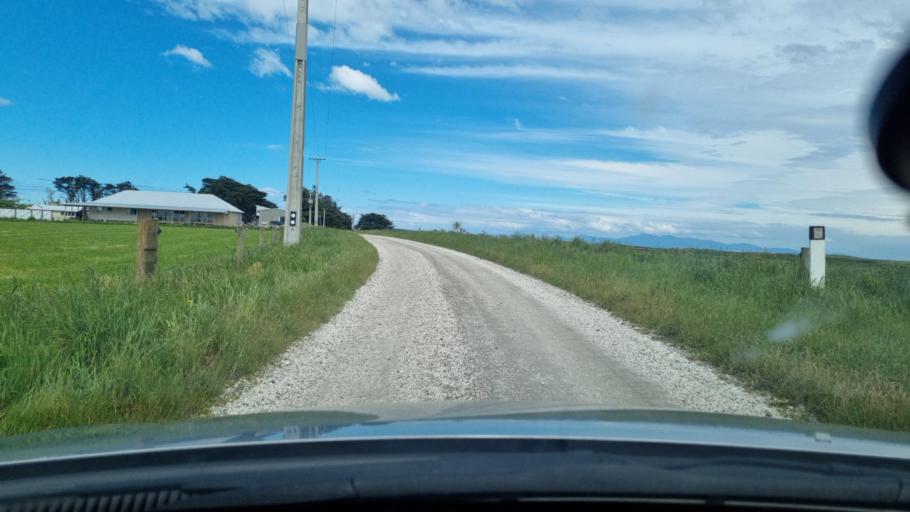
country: NZ
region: Southland
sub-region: Invercargill City
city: Invercargill
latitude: -46.3991
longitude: 168.2564
